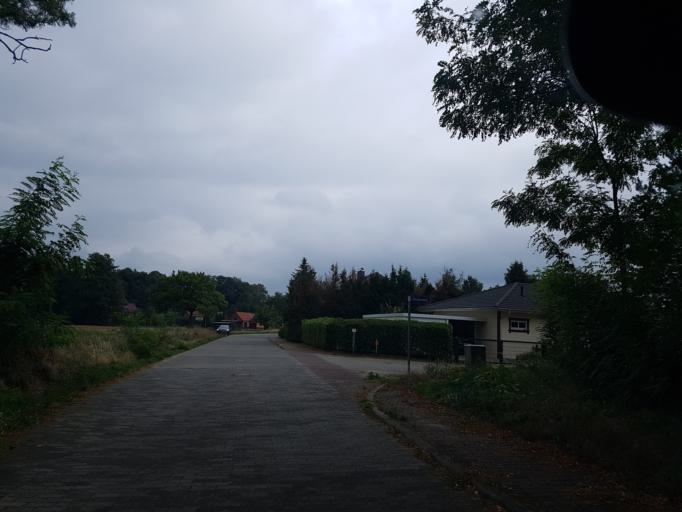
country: DE
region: Saxony-Anhalt
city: Loburg
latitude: 52.2437
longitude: 12.0472
